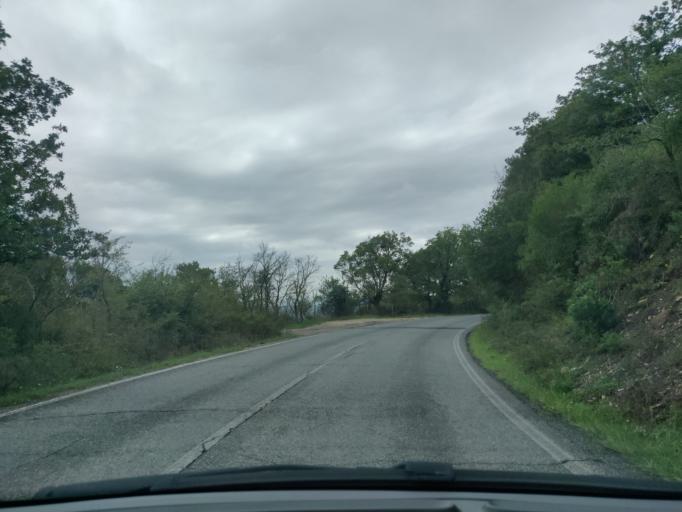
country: IT
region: Latium
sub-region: Citta metropolitana di Roma Capitale
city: Allumiere
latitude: 42.1371
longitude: 11.8716
